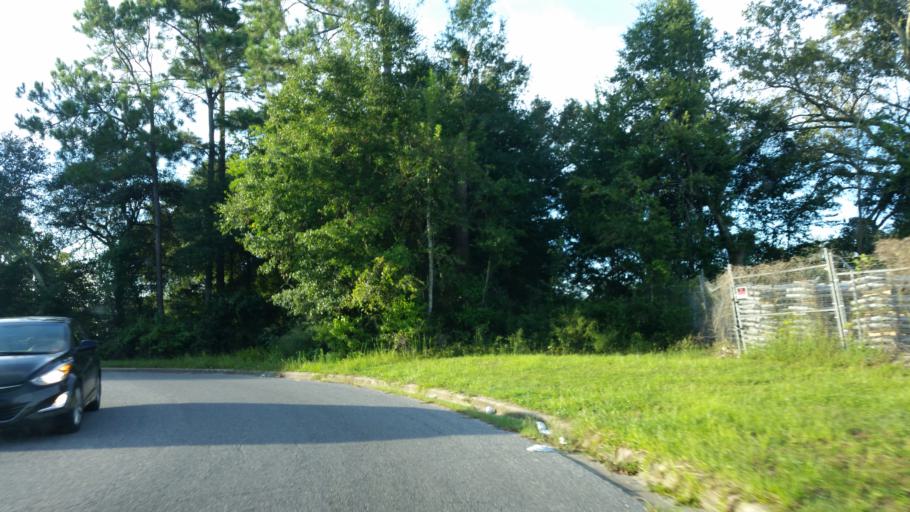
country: US
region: Florida
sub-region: Escambia County
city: Brent
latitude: 30.4740
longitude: -87.2655
